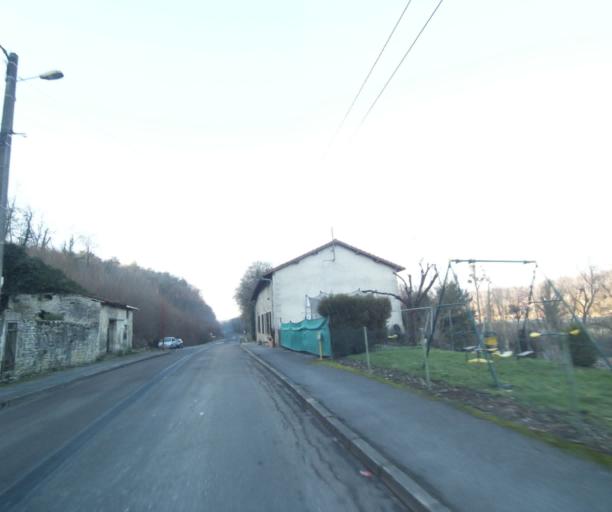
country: FR
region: Champagne-Ardenne
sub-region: Departement de la Haute-Marne
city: Bienville
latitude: 48.5497
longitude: 5.0713
